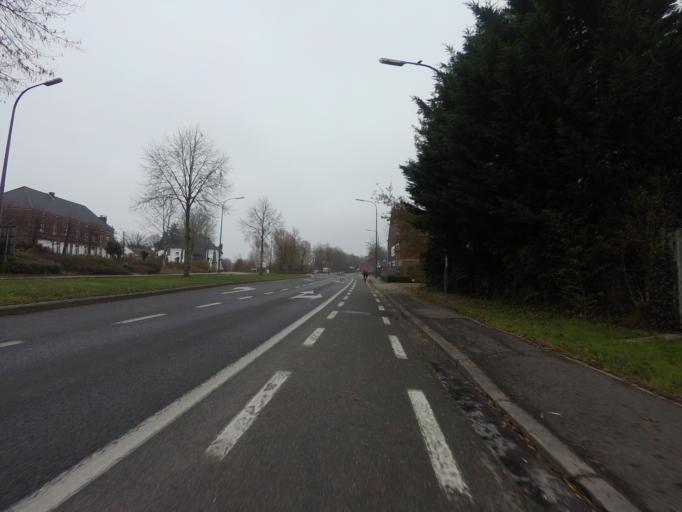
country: BE
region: Flanders
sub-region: Provincie Oost-Vlaanderen
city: Geraardsbergen
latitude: 50.7779
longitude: 3.8747
